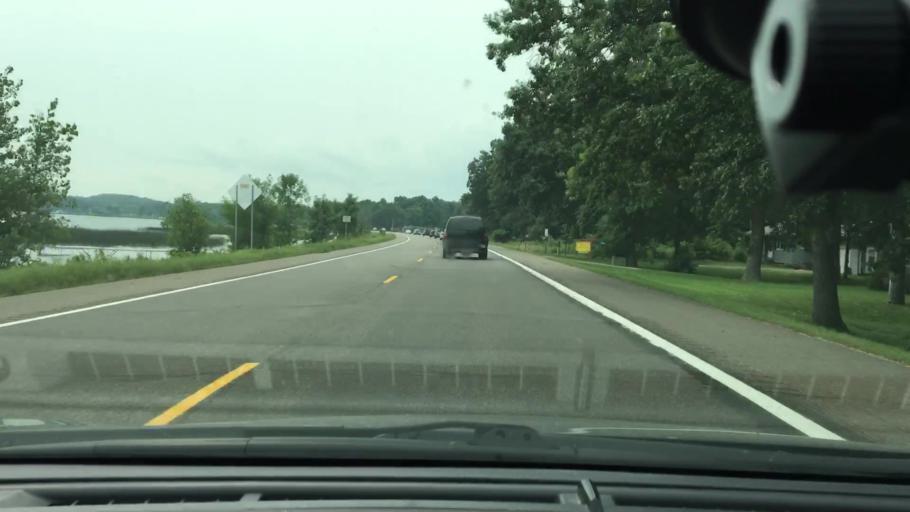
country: US
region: Minnesota
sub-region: Mille Lacs County
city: Vineland
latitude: 46.2625
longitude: -93.8242
